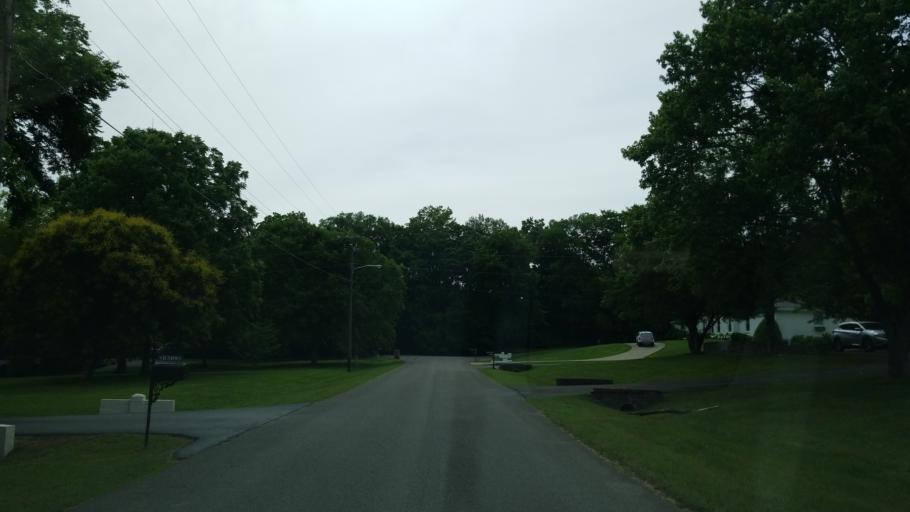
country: US
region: Tennessee
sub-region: Davidson County
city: Forest Hills
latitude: 36.0394
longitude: -86.8335
